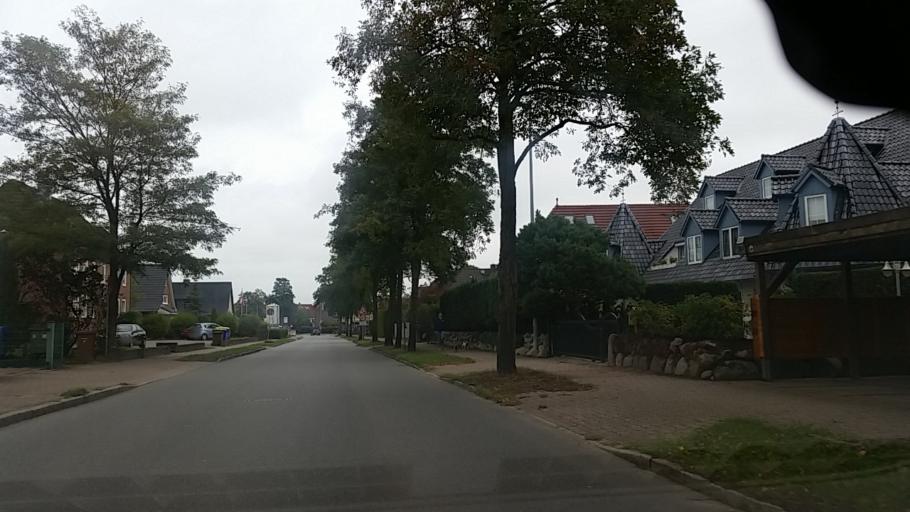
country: DE
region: Schleswig-Holstein
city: Kaltenkirchen
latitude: 53.8410
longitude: 9.9594
